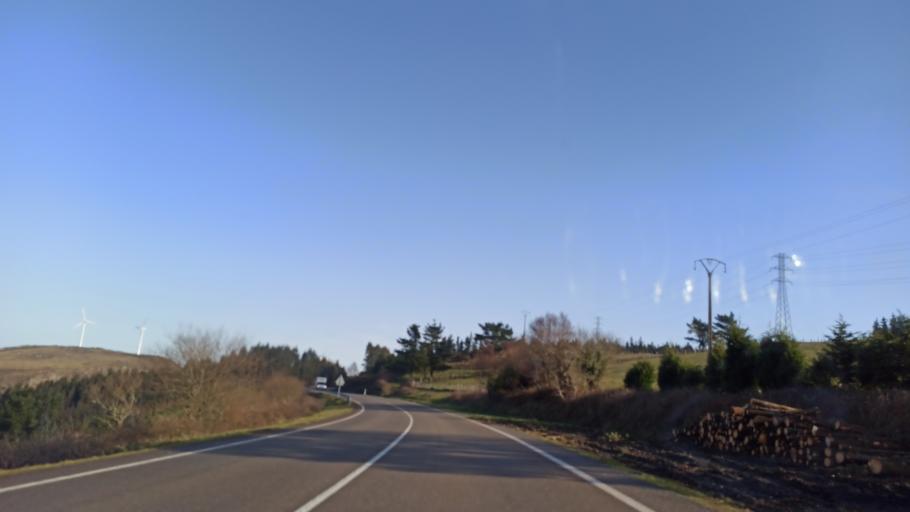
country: ES
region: Galicia
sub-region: Provincia da Coruna
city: As Pontes de Garcia Rodriguez
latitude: 43.5274
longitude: -7.8126
